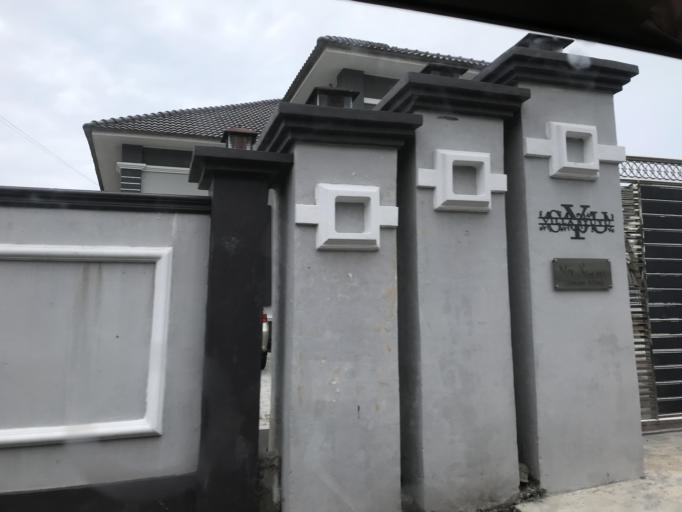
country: MY
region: Kelantan
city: Kota Bharu
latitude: 6.1165
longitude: 102.2087
